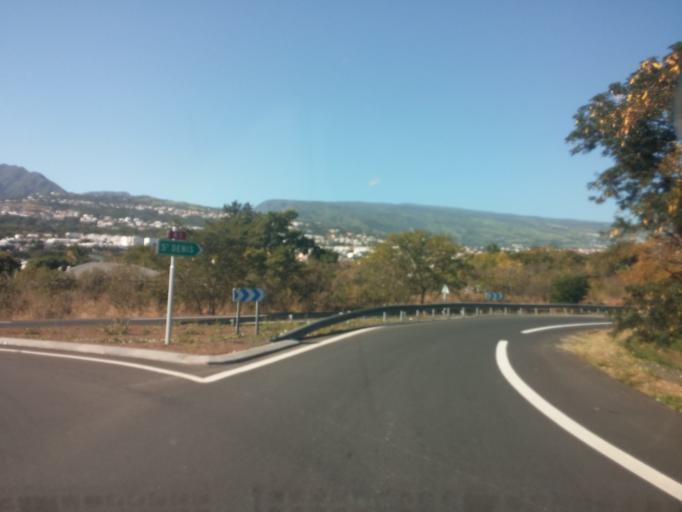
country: RE
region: Reunion
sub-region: Reunion
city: La Possession
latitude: -20.9458
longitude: 55.3256
